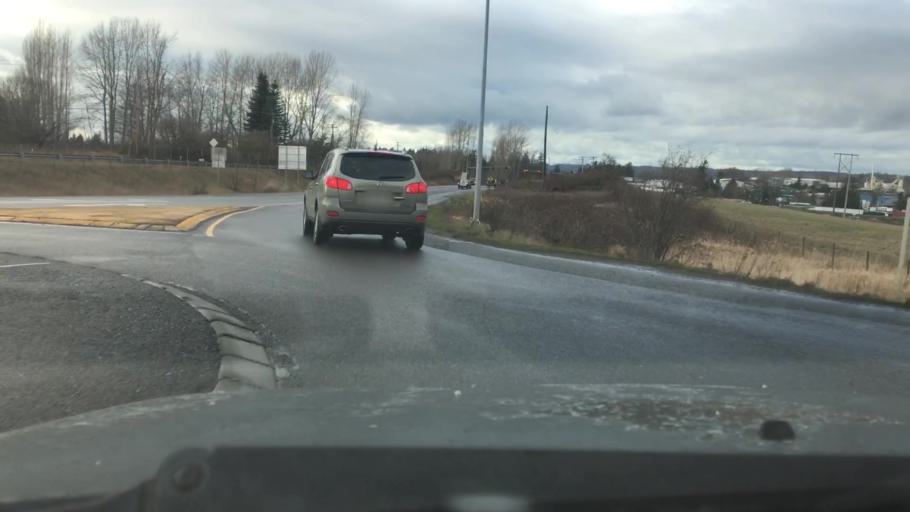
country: US
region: Washington
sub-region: Whatcom County
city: Marietta-Alderwood
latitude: 48.8172
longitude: -122.5506
